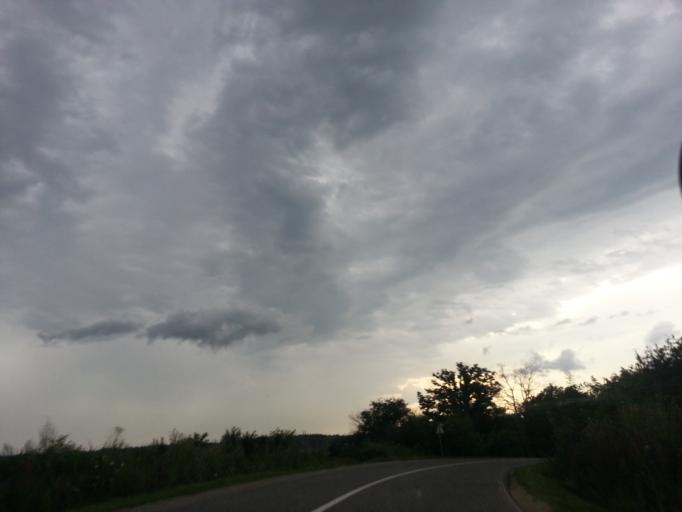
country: BA
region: Republika Srpska
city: Velika Obarska
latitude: 44.7812
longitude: 19.0994
